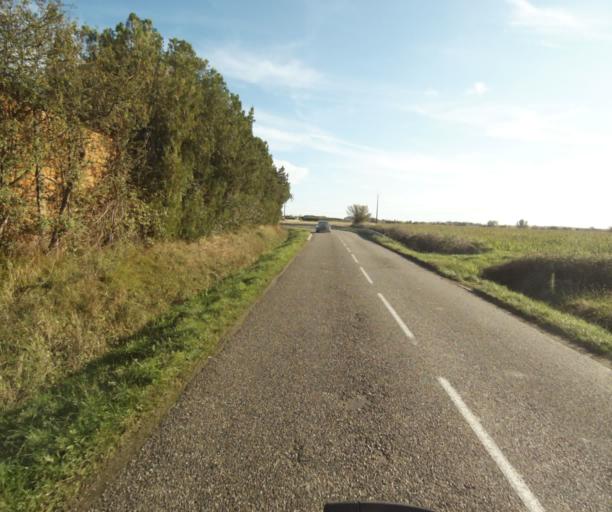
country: FR
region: Midi-Pyrenees
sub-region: Departement du Tarn-et-Garonne
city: Finhan
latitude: 43.8993
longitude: 1.1249
